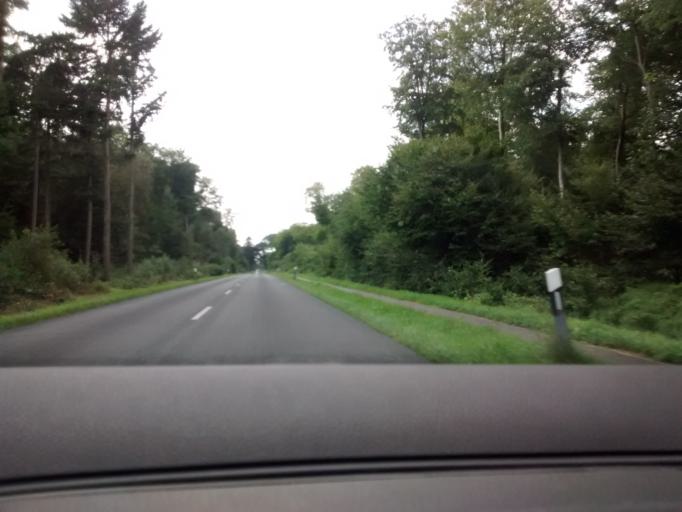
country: DE
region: Lower Saxony
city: Brietlingen
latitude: 53.3167
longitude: 10.4823
